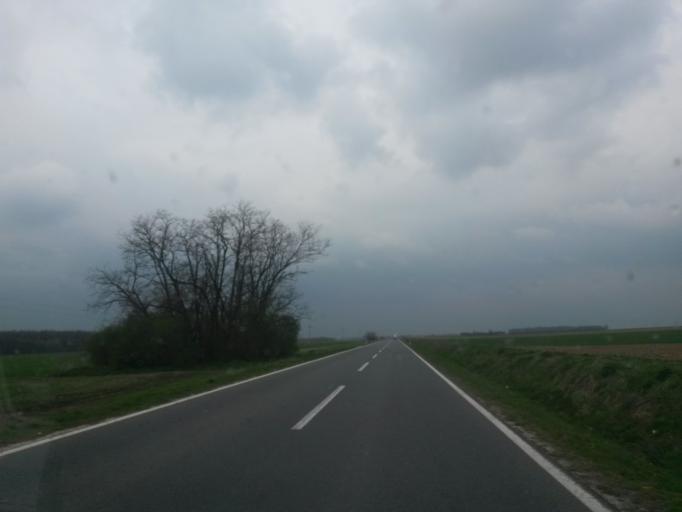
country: HR
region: Vukovarsko-Srijemska
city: Slakovci
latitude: 45.2018
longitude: 19.0113
